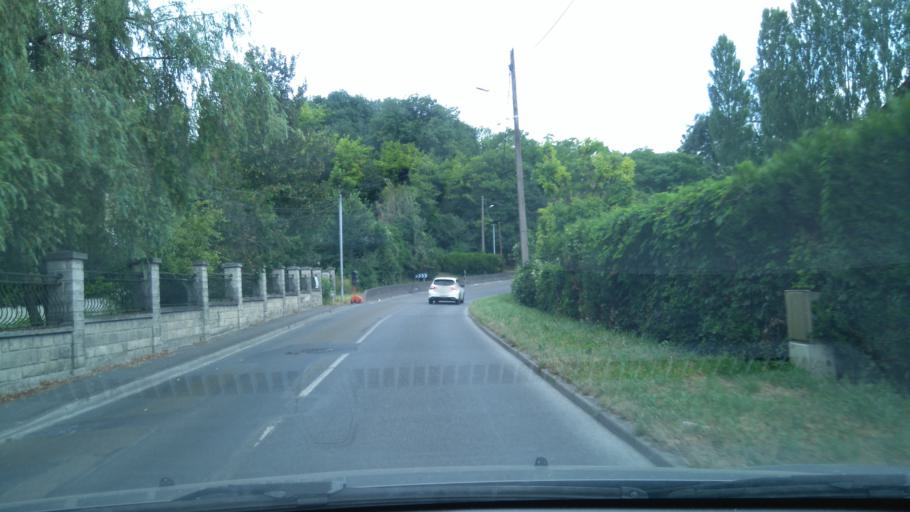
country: FR
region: Picardie
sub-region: Departement de l'Oise
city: Gouvieux
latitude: 49.2002
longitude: 2.4252
